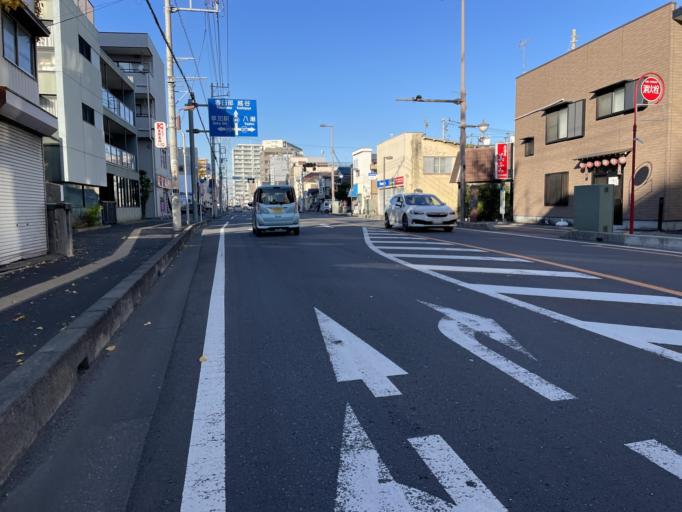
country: JP
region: Saitama
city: Soka
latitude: 35.8274
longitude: 139.8073
